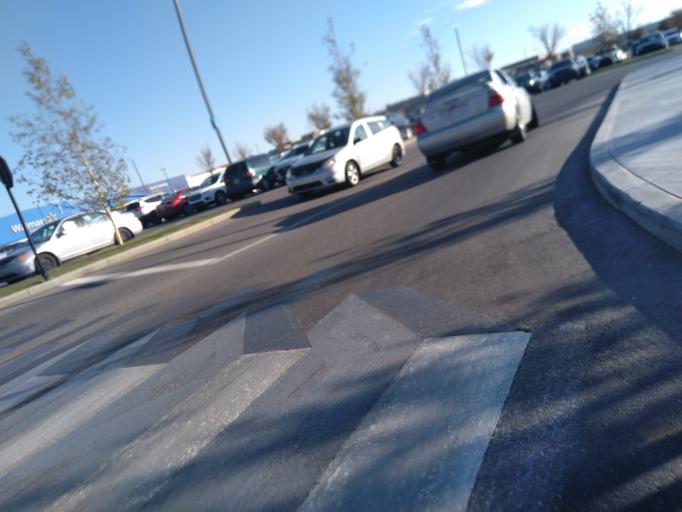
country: CA
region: Alberta
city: Calgary
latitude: 51.1084
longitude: -114.0403
